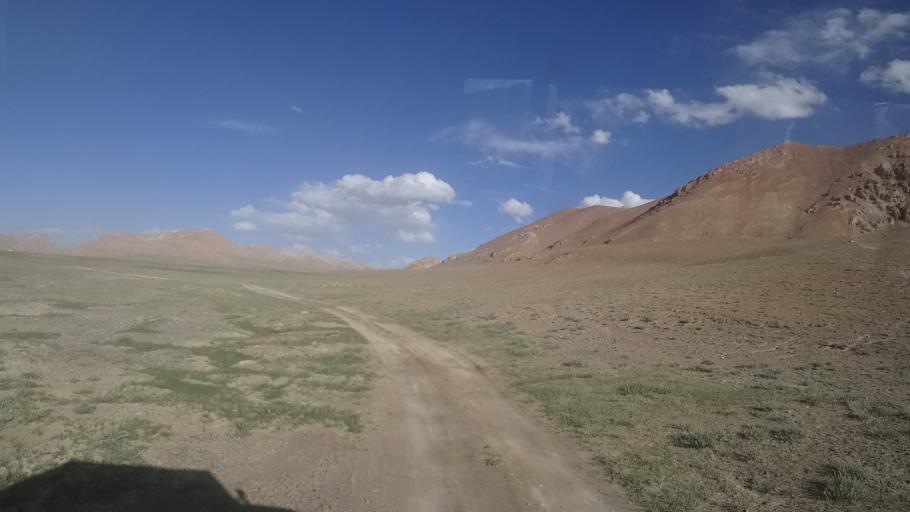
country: TJ
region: Gorno-Badakhshan
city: Murghob
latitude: 37.6562
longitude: 74.1671
